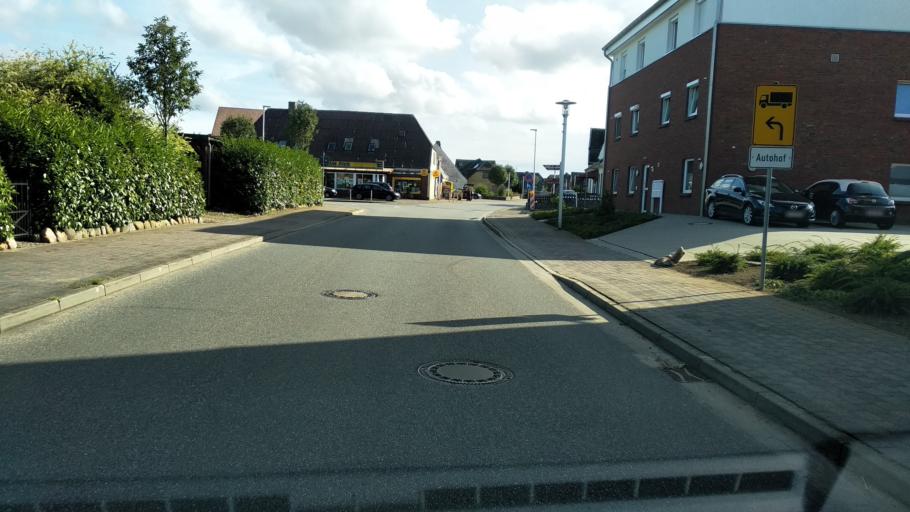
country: DE
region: Schleswig-Holstein
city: Busdorf
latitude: 54.4932
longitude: 9.5531
